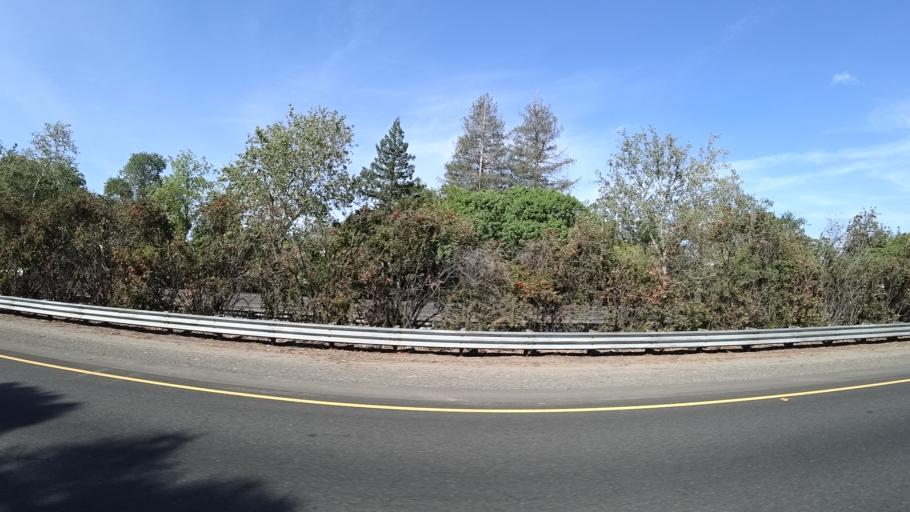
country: US
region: California
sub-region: Butte County
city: Chico
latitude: 39.7501
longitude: -121.8382
